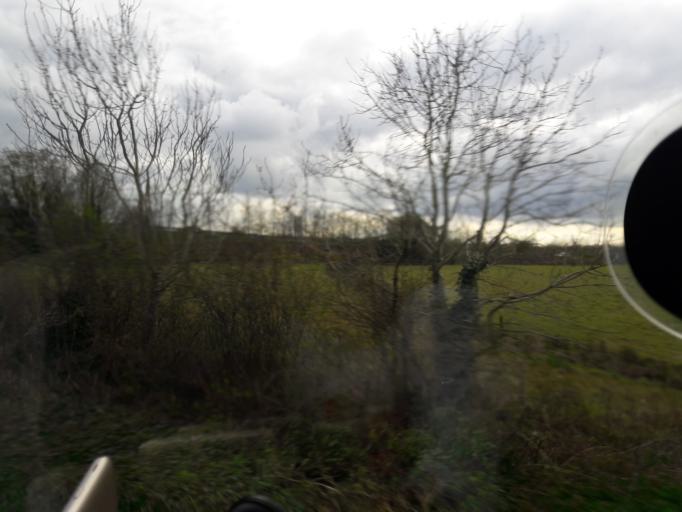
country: IE
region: Leinster
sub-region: An Longfort
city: Longford
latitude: 53.7254
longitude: -7.8151
